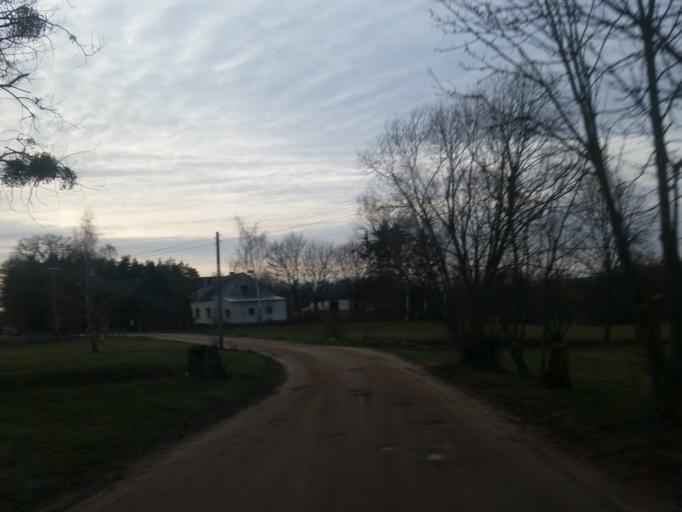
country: PL
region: Kujawsko-Pomorskie
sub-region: Powiat brodnicki
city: Brodnica
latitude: 53.2220
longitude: 19.3461
